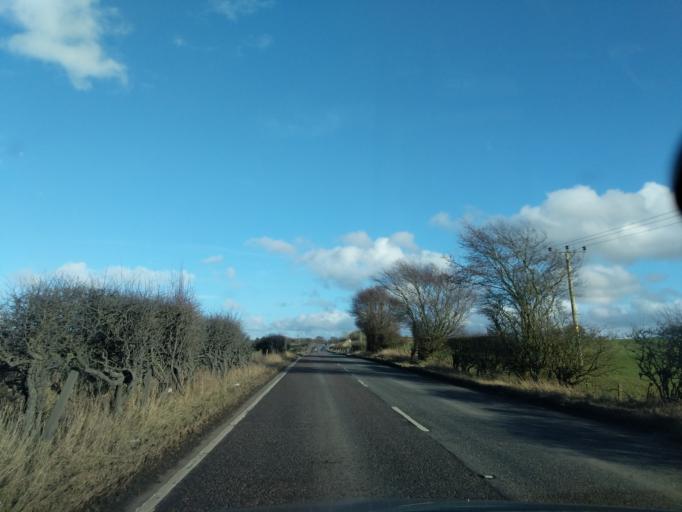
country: GB
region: Scotland
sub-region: North Lanarkshire
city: Shotts
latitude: 55.8082
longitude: -3.8006
